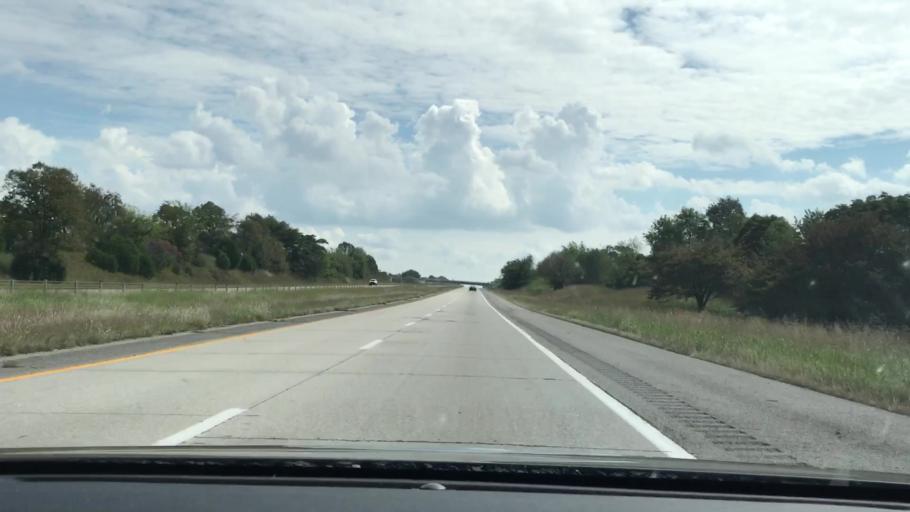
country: US
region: Kentucky
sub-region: Trigg County
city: Cadiz
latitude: 36.8982
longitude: -87.7631
